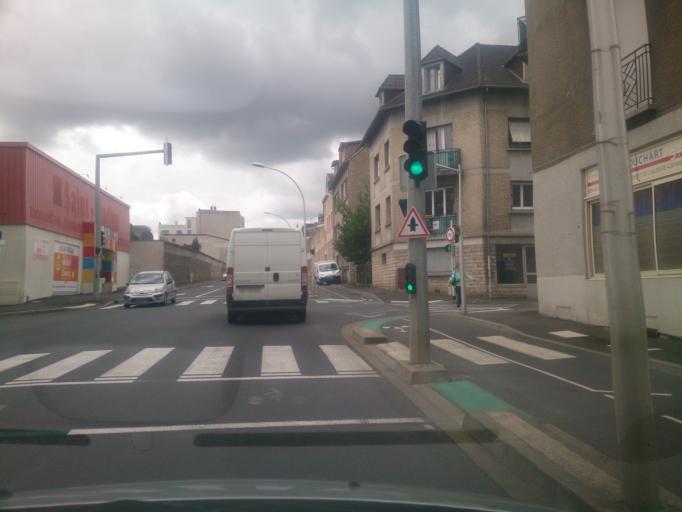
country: FR
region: Limousin
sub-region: Departement de la Correze
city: Brive-la-Gaillarde
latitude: 45.1592
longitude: 1.5406
